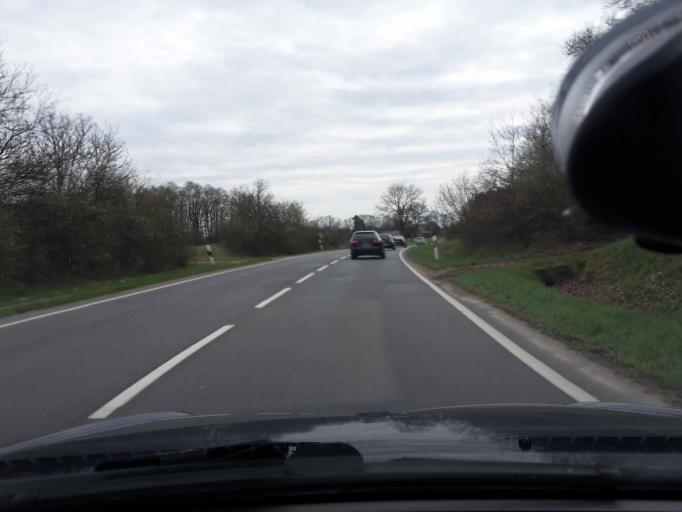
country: DE
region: Lower Saxony
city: Harmstorf
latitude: 53.3553
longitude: 9.9909
